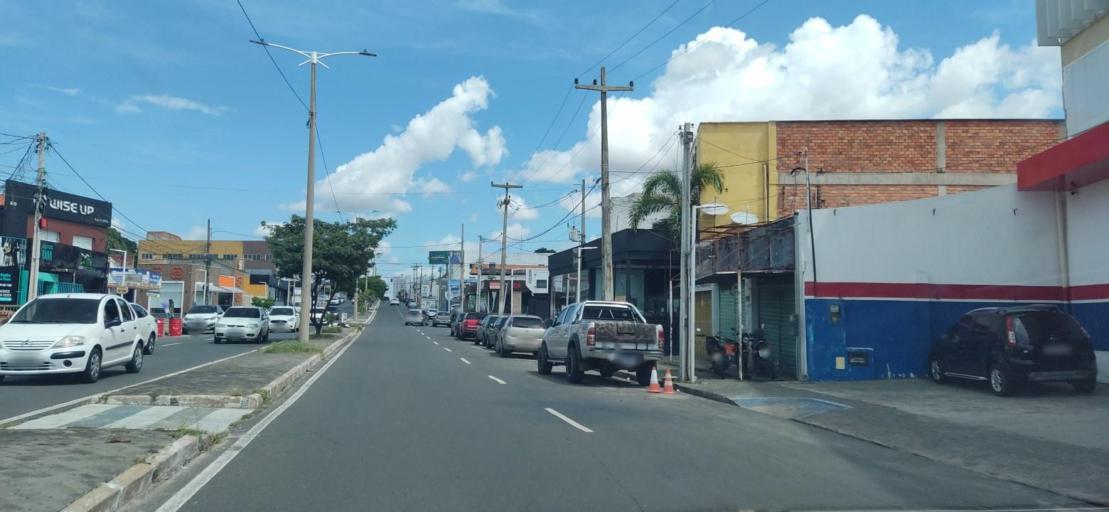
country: BR
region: Piaui
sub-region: Teresina
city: Teresina
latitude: -5.0649
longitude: -42.7938
